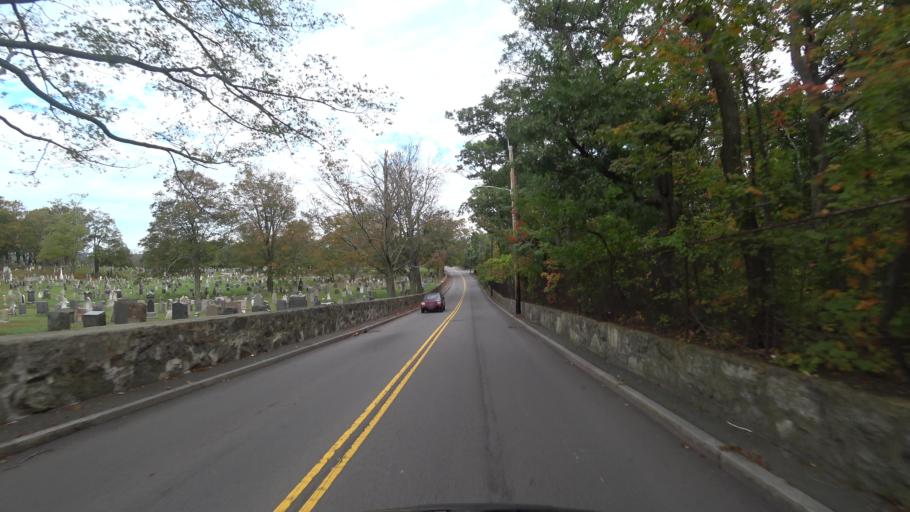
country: US
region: Massachusetts
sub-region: Suffolk County
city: Jamaica Plain
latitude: 42.2763
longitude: -71.1082
